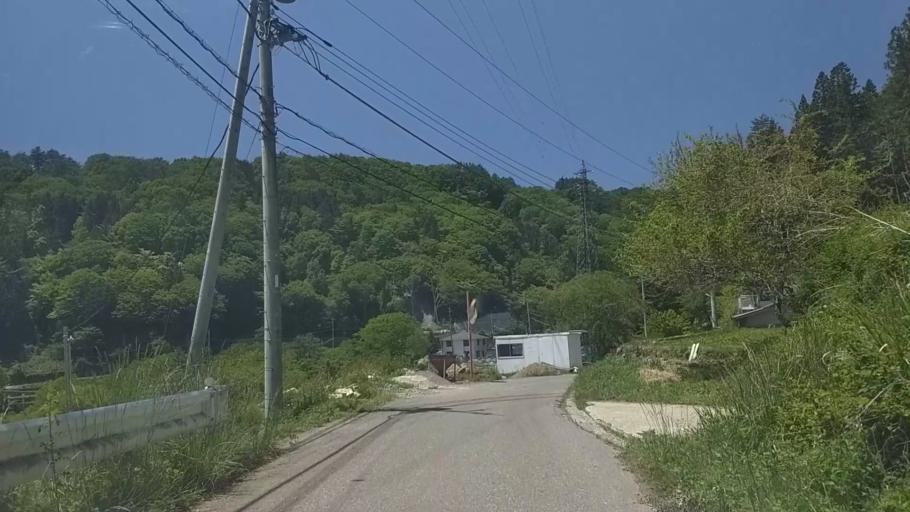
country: JP
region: Yamanashi
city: Nirasaki
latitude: 35.8764
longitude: 138.4314
